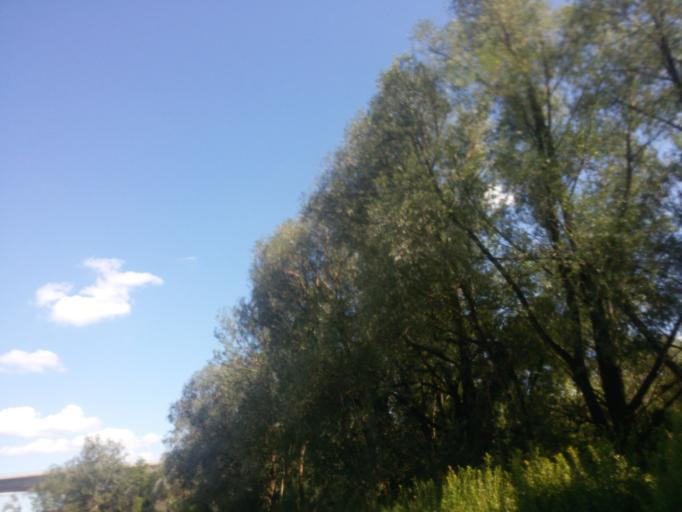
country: AT
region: Carinthia
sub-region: Villach Stadt
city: Villach
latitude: 46.6075
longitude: 13.8877
